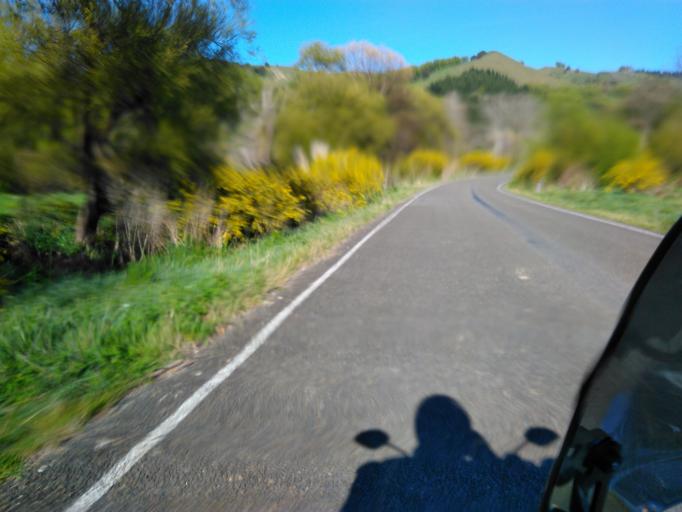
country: NZ
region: Gisborne
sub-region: Gisborne District
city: Gisborne
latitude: -38.4436
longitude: 177.7591
